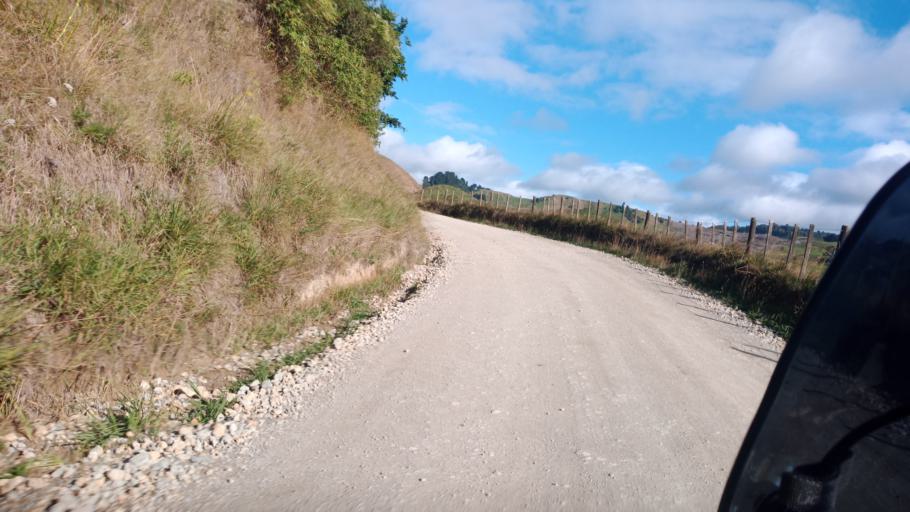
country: NZ
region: Gisborne
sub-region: Gisborne District
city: Gisborne
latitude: -38.5385
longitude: 177.5154
